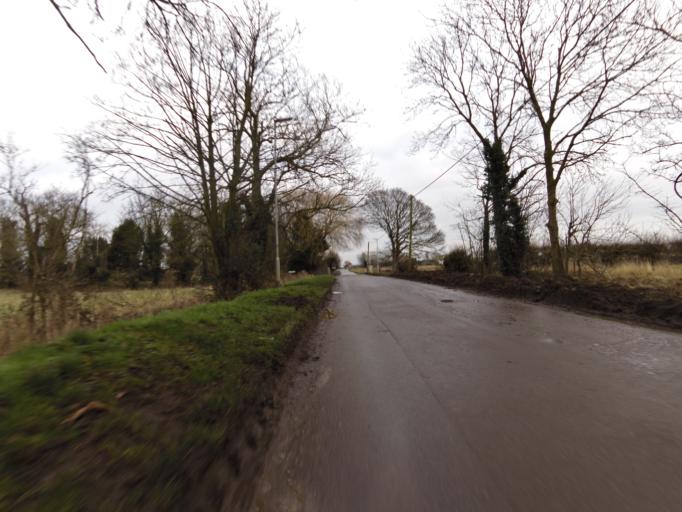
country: GB
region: England
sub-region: Cambridgeshire
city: Waterbeach
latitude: 52.2702
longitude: 0.2005
